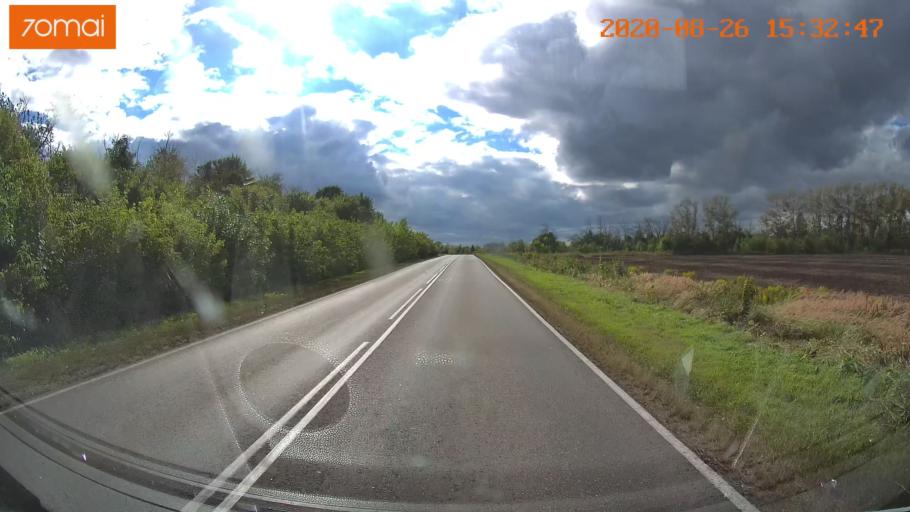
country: RU
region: Tula
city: Severo-Zadonsk
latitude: 54.0741
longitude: 38.3555
